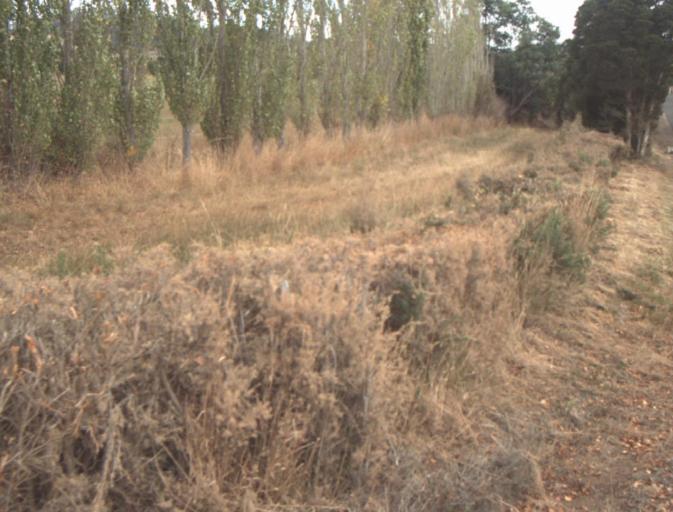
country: AU
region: Tasmania
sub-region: Launceston
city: Mayfield
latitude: -41.2901
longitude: 146.9907
